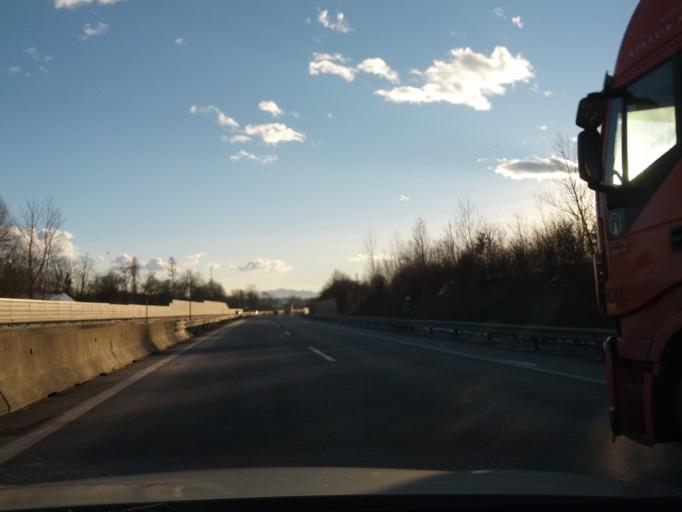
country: SI
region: Dol pri Ljubljani
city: Dol pri Ljubljani
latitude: 46.1131
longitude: 14.6016
